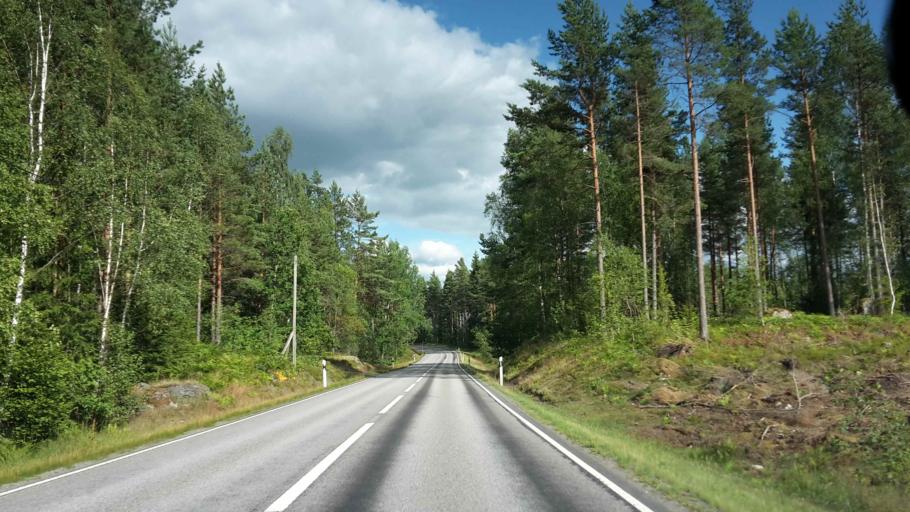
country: SE
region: OEstergoetland
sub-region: Motala Kommun
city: Borensberg
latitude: 58.8018
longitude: 15.4304
